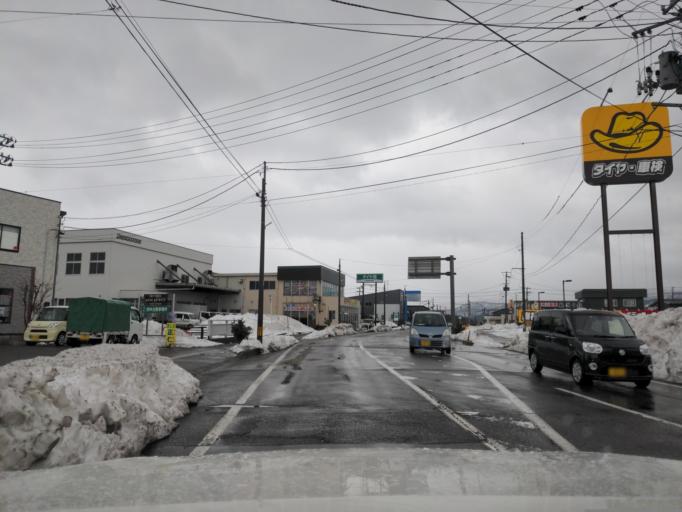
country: JP
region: Niigata
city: Kashiwazaki
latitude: 37.3606
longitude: 138.5639
